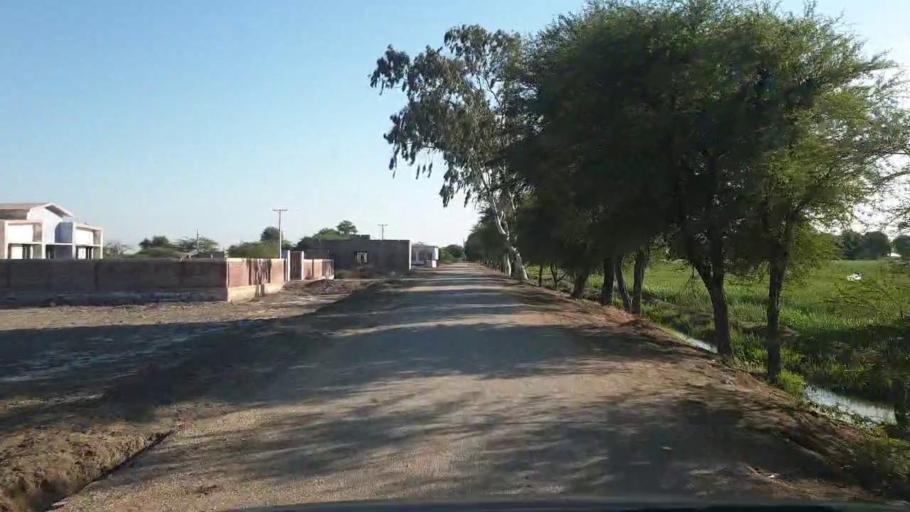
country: PK
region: Sindh
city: Dhoro Naro
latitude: 25.4303
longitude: 69.5388
